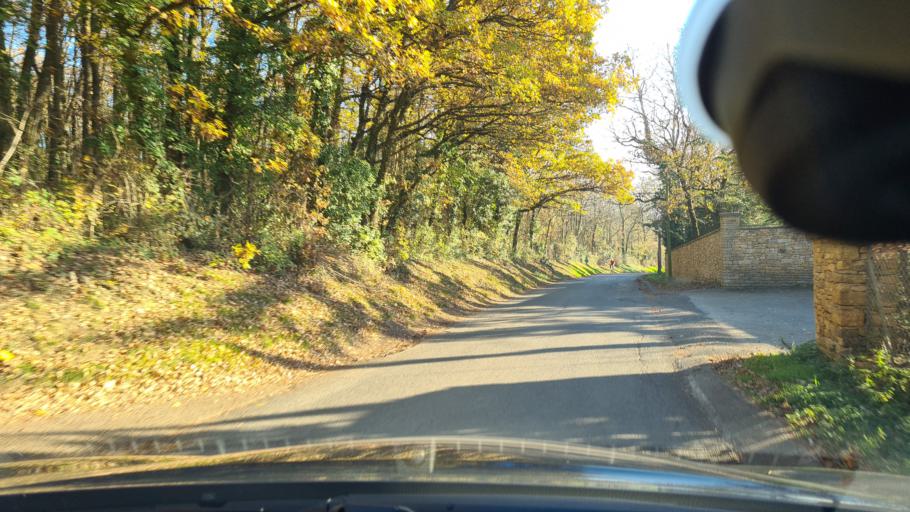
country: FR
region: Rhone-Alpes
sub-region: Departement du Rhone
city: Limonest
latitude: 45.8298
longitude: 4.8092
